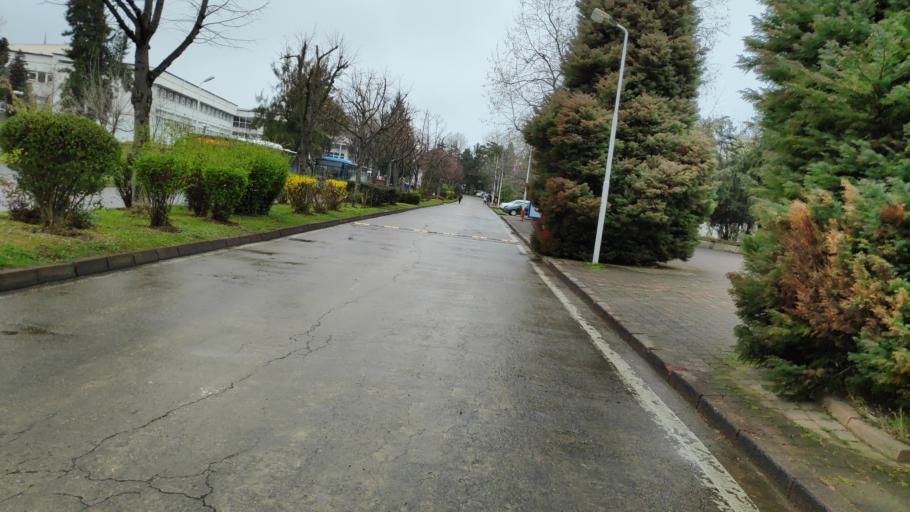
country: TR
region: Trabzon
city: Trabzon
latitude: 40.9930
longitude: 39.7759
